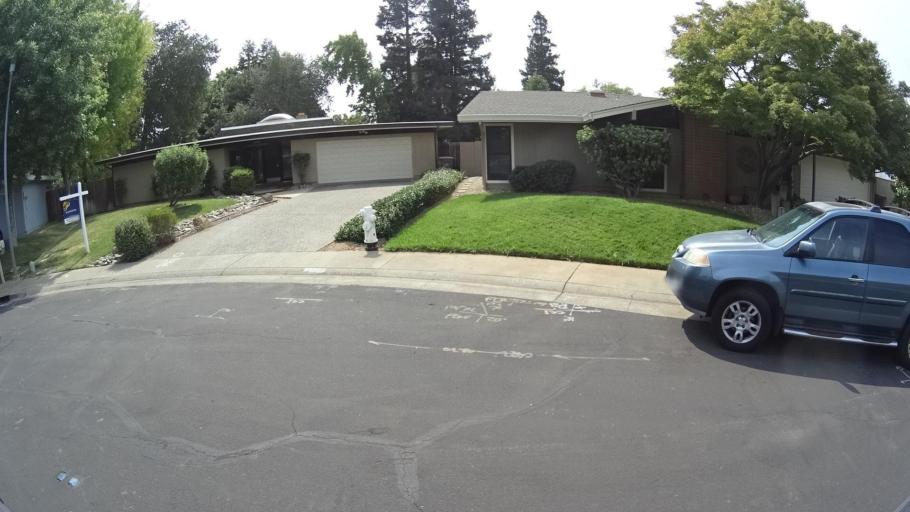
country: US
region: California
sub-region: Sacramento County
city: Elk Grove
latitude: 38.4147
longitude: -121.3782
